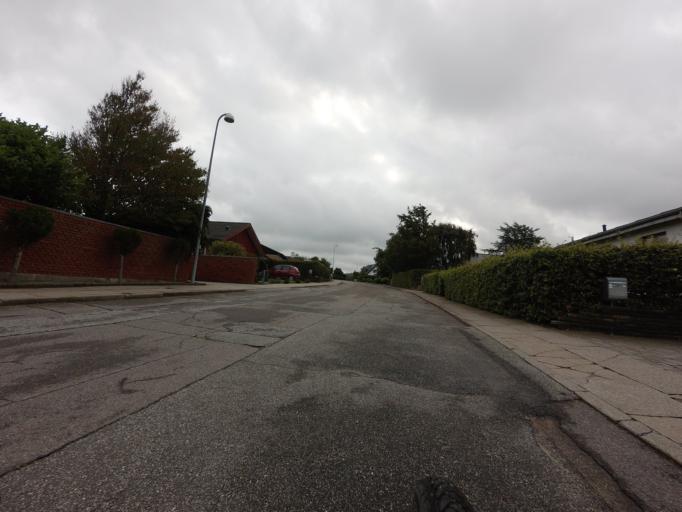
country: DK
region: North Denmark
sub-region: Hjorring Kommune
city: Hjorring
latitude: 57.4692
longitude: 9.9779
